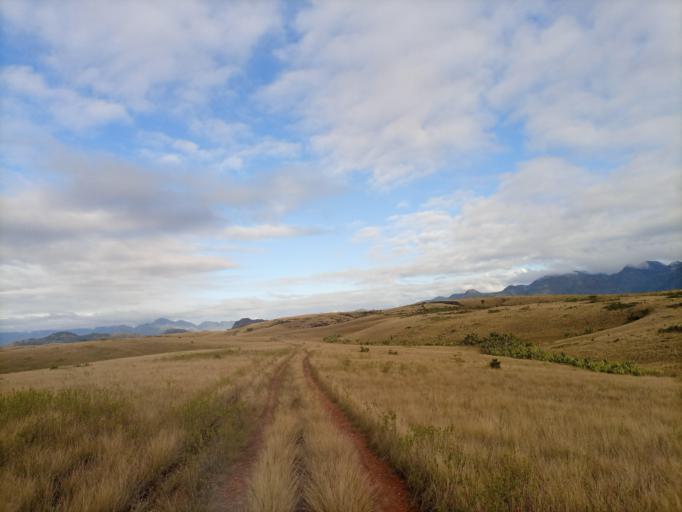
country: MG
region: Anosy
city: Fort Dauphin
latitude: -24.3109
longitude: 47.2429
